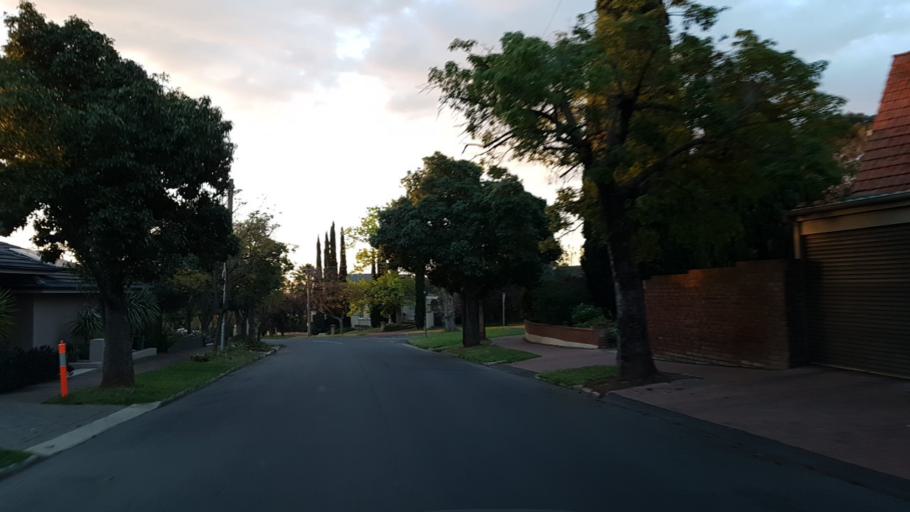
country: AU
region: South Australia
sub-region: Burnside
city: Linden Park
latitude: -34.9501
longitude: 138.6459
